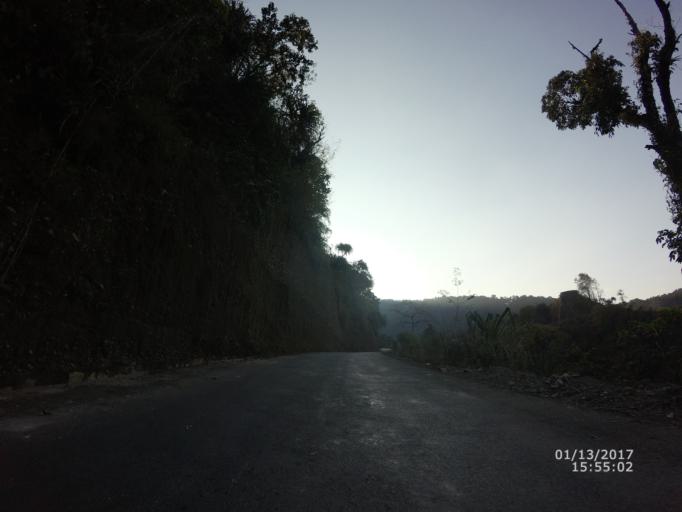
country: NP
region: Western Region
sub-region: Gandaki Zone
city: Pokhara
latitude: 28.1595
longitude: 84.0069
